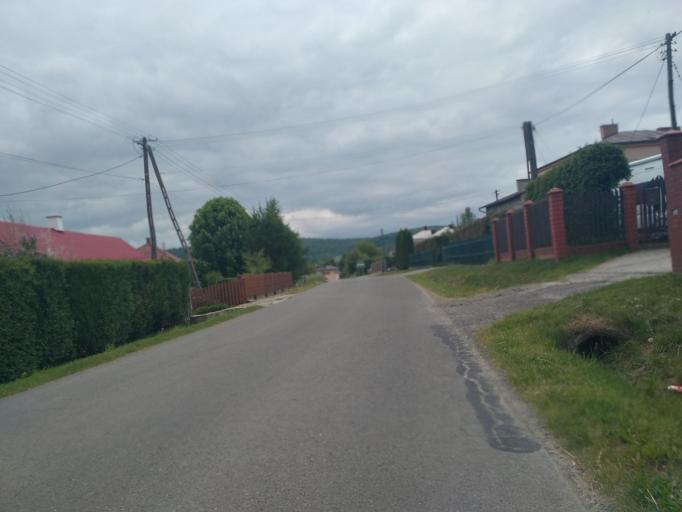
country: PL
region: Subcarpathian Voivodeship
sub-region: Powiat krosnienski
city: Jedlicze
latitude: 49.6983
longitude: 21.6395
